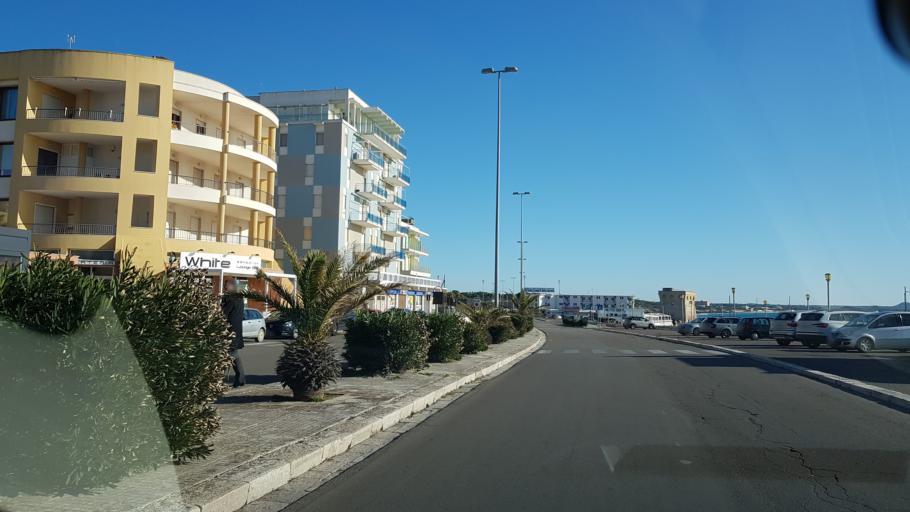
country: IT
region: Apulia
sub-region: Provincia di Lecce
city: Gallipoli
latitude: 40.0495
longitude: 18.0004
